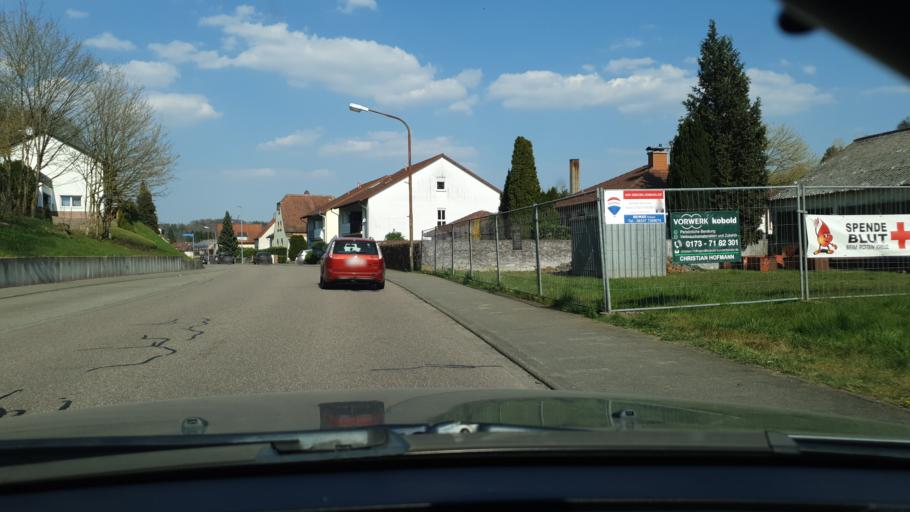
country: DE
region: Rheinland-Pfalz
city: Contwig
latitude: 49.2702
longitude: 7.4158
